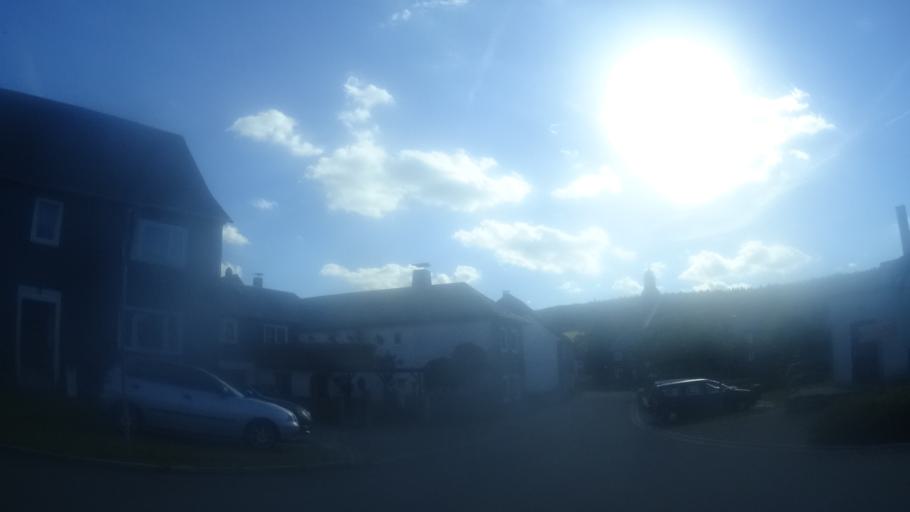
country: DE
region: Thuringia
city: Herschdorf
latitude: 50.6286
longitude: 11.0507
